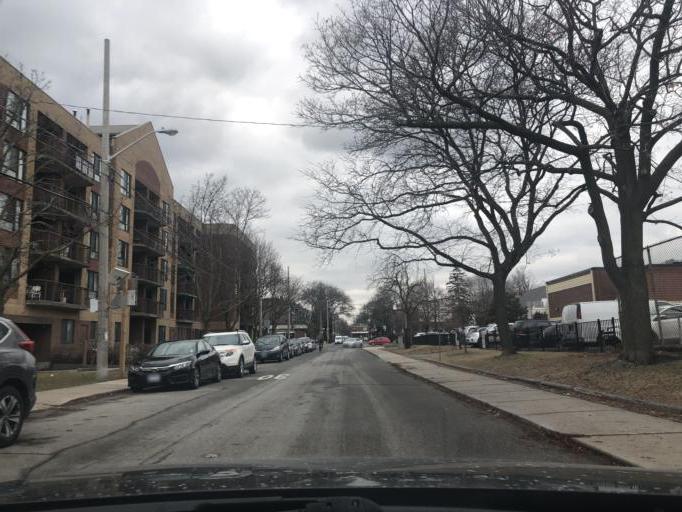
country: CA
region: Ontario
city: Toronto
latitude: 43.6815
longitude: -79.3364
